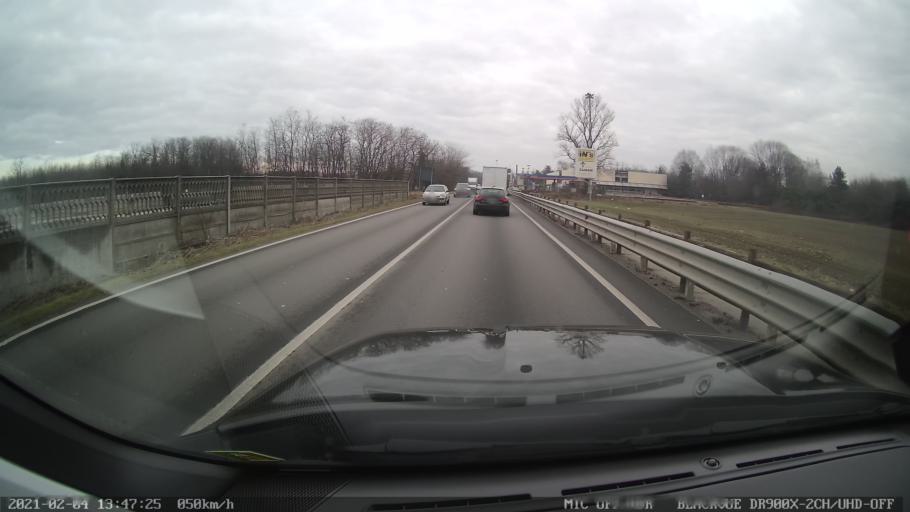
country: IT
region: Lombardy
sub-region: Provincia di Varese
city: Solbiate Olona
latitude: 45.6447
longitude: 8.8641
